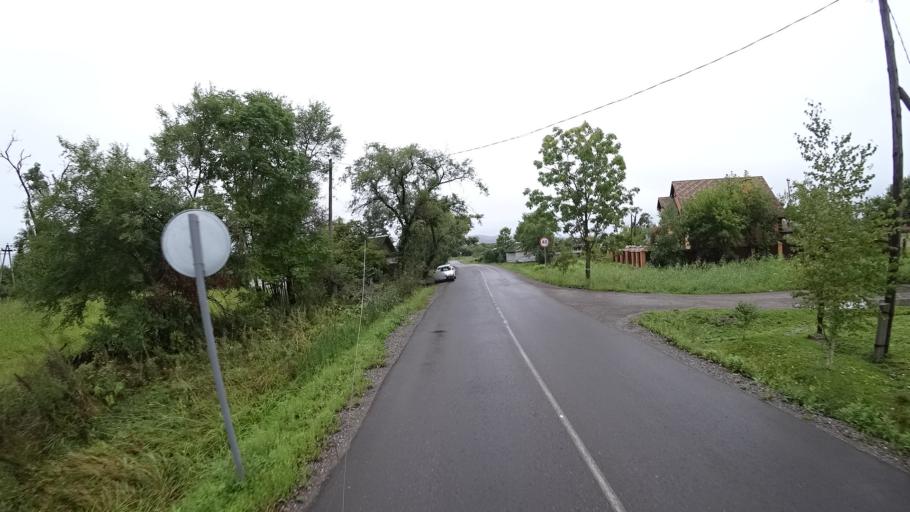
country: RU
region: Primorskiy
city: Monastyrishche
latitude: 44.2052
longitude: 132.4354
